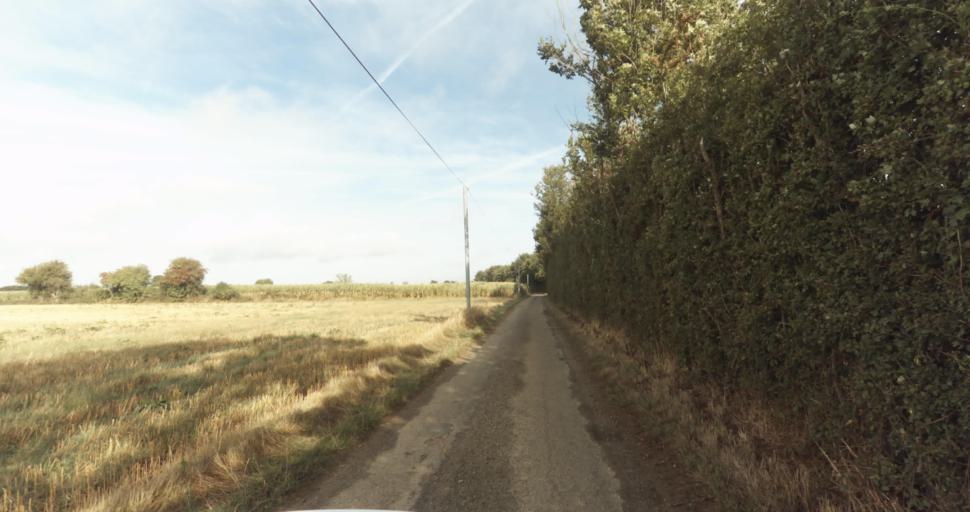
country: FR
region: Lower Normandy
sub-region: Departement de l'Orne
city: Gace
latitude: 48.8705
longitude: 0.3362
